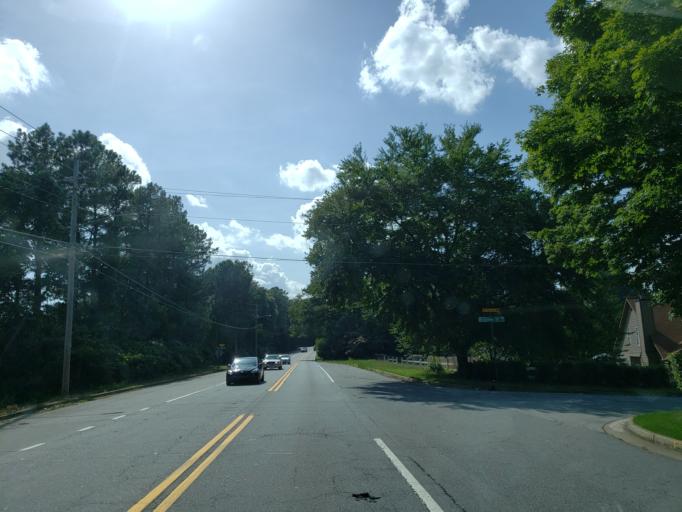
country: US
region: Georgia
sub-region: Cobb County
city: Mableton
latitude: 33.8670
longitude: -84.6045
